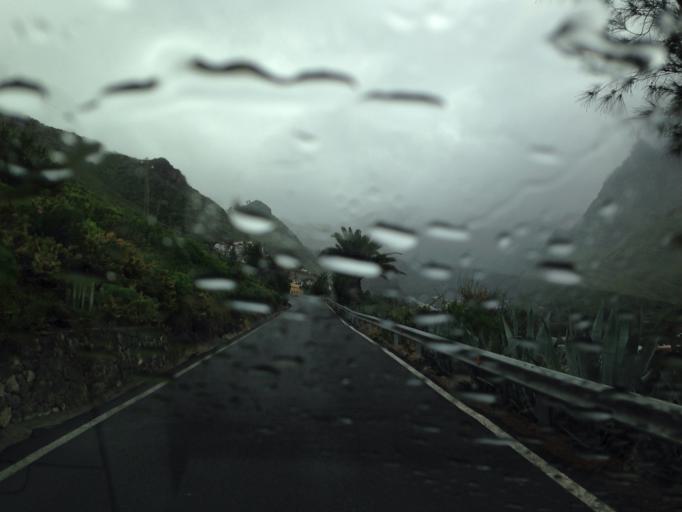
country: ES
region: Canary Islands
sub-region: Provincia de Las Palmas
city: Agaete
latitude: 28.0938
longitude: -15.6829
